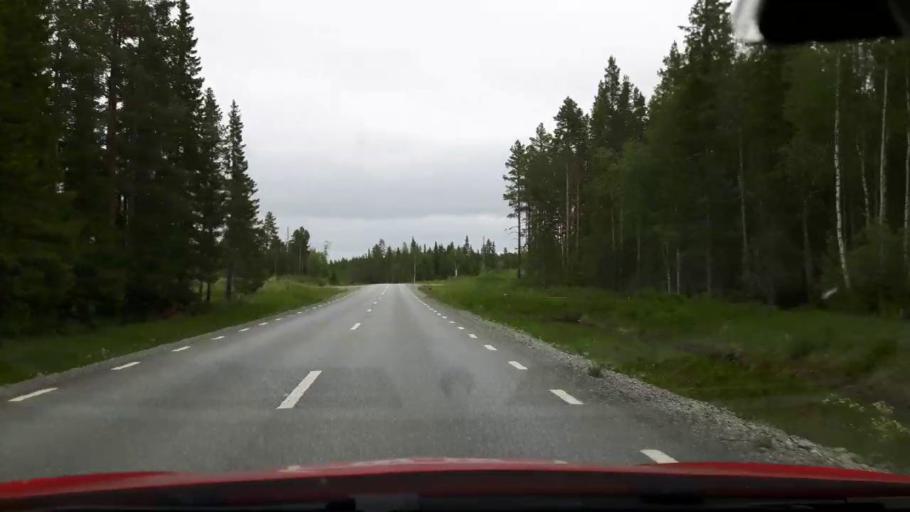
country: SE
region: Jaemtland
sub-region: OEstersunds Kommun
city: Lit
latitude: 63.6913
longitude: 14.6788
